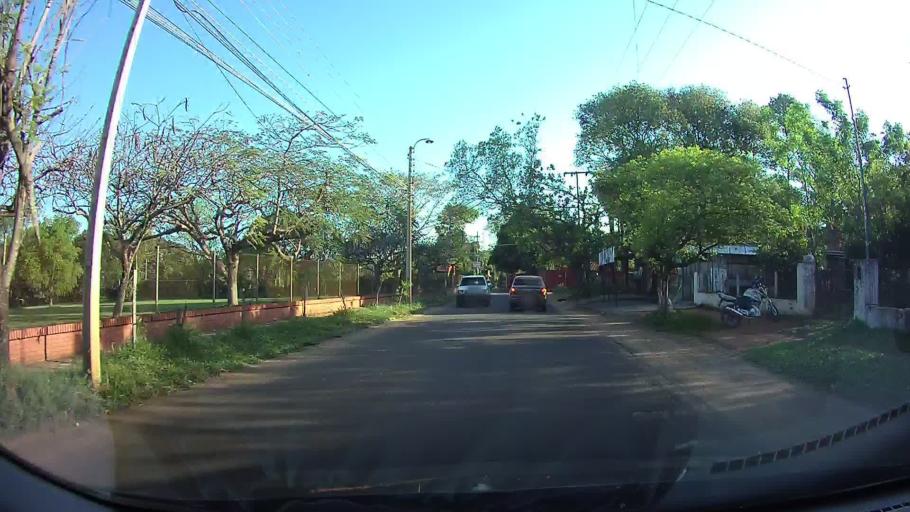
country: PY
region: Central
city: Fernando de la Mora
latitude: -25.3431
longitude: -57.5323
